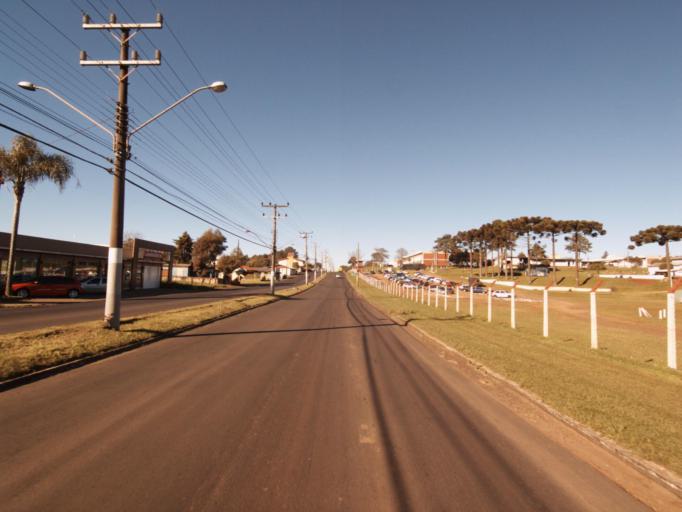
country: AR
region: Misiones
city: Bernardo de Irigoyen
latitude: -26.7550
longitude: -53.5007
